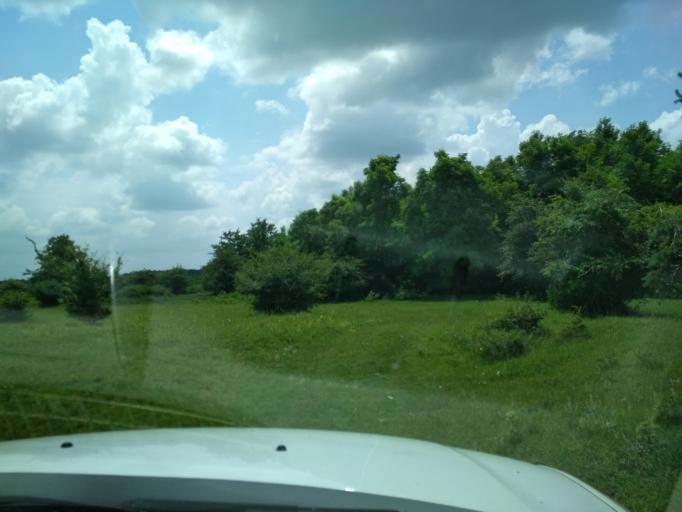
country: HU
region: Pest
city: Tapiosag
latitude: 47.4153
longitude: 19.6539
